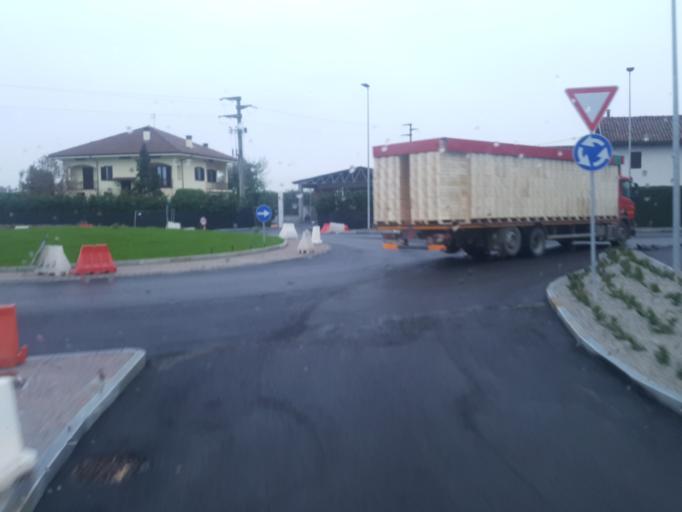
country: IT
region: Piedmont
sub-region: Provincia di Cuneo
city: Saluzzo
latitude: 44.6395
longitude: 7.5074
